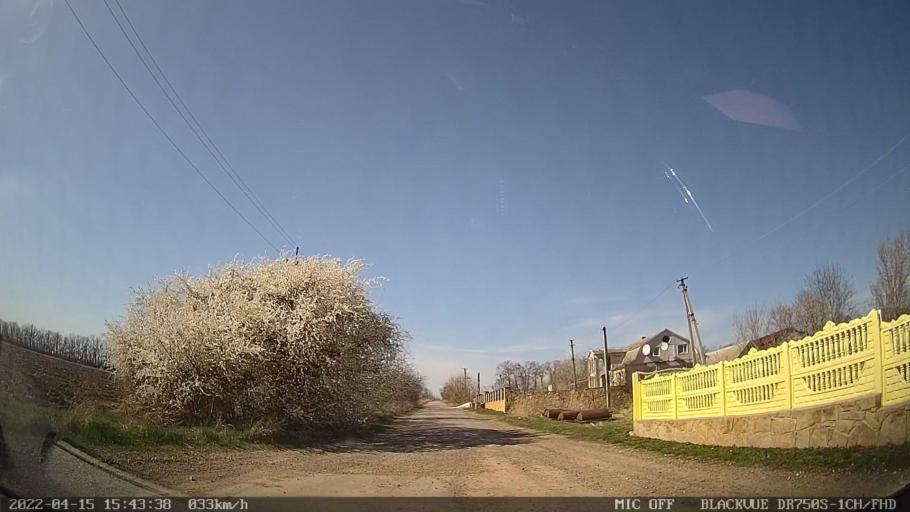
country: MD
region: Raionul Ocnita
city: Otaci
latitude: 48.3660
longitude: 27.9257
